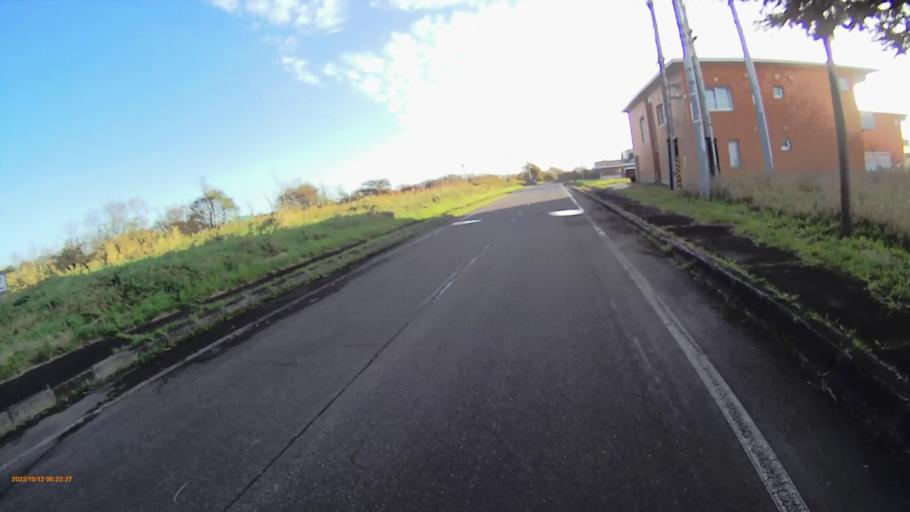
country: JP
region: Hokkaido
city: Kushiro
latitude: 42.8878
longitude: 143.9356
